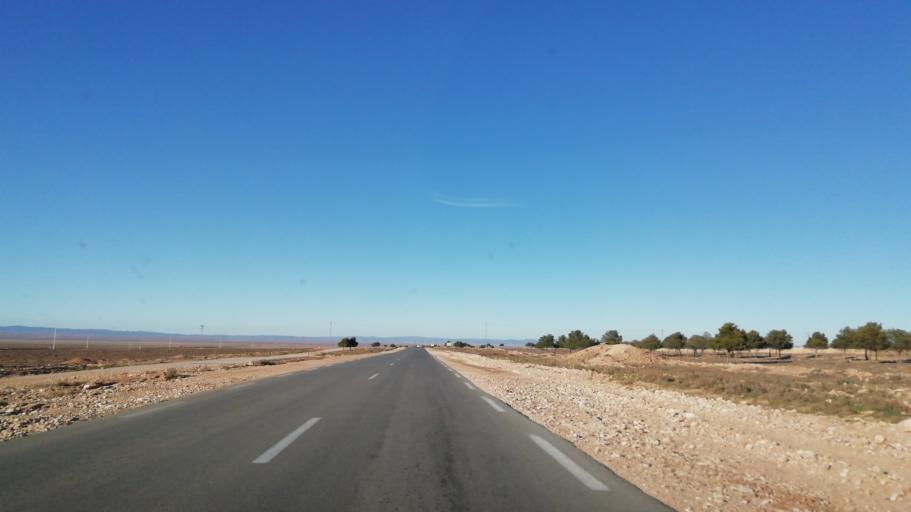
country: DZ
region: Tlemcen
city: Sebdou
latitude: 34.2959
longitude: -1.2607
